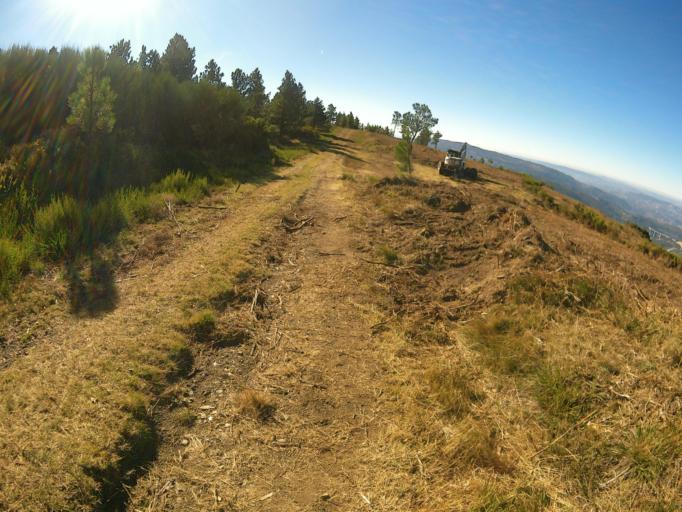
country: PT
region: Vila Real
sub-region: Mesao Frio
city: Mesao Frio
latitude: 41.2481
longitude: -7.9209
